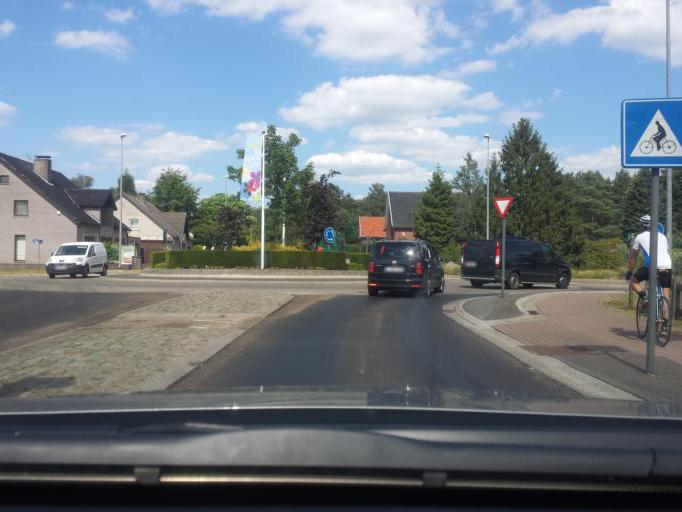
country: BE
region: Flanders
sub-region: Provincie Limburg
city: Beringen
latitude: 51.0654
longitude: 5.2042
